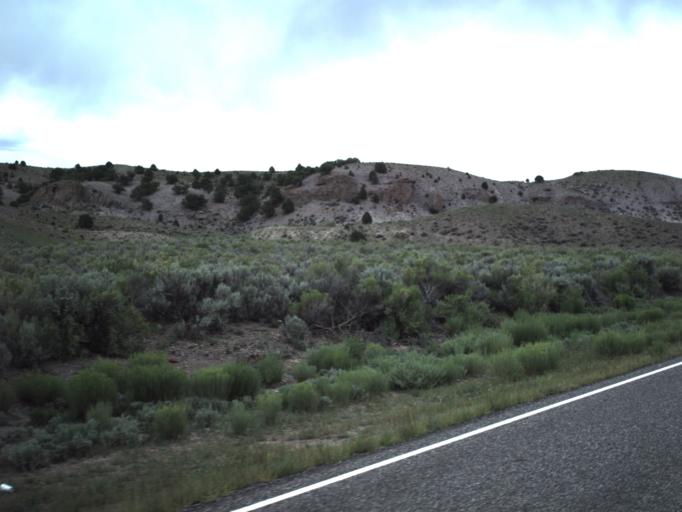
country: US
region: Utah
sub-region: Piute County
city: Junction
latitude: 38.1749
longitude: -112.0645
